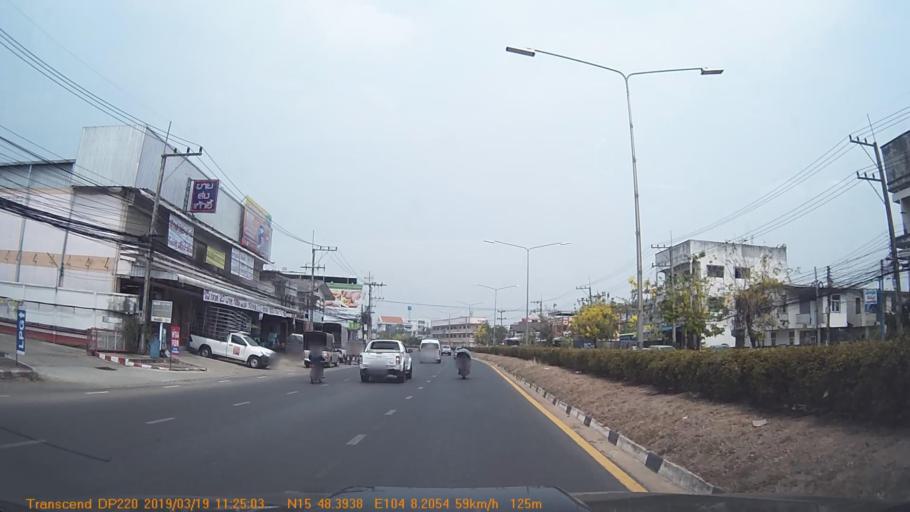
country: TH
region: Yasothon
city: Yasothon
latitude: 15.8067
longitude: 104.1367
